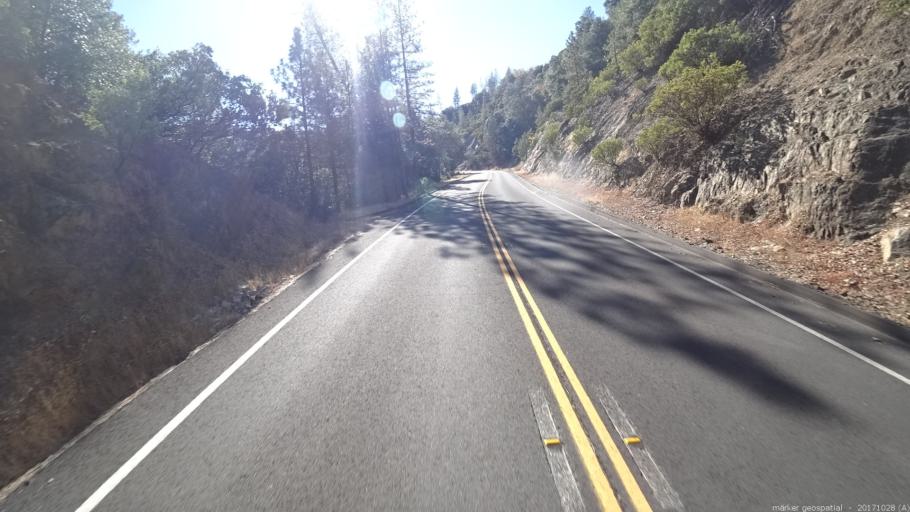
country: US
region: California
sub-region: Shasta County
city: Shasta
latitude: 40.6133
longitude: -122.5652
